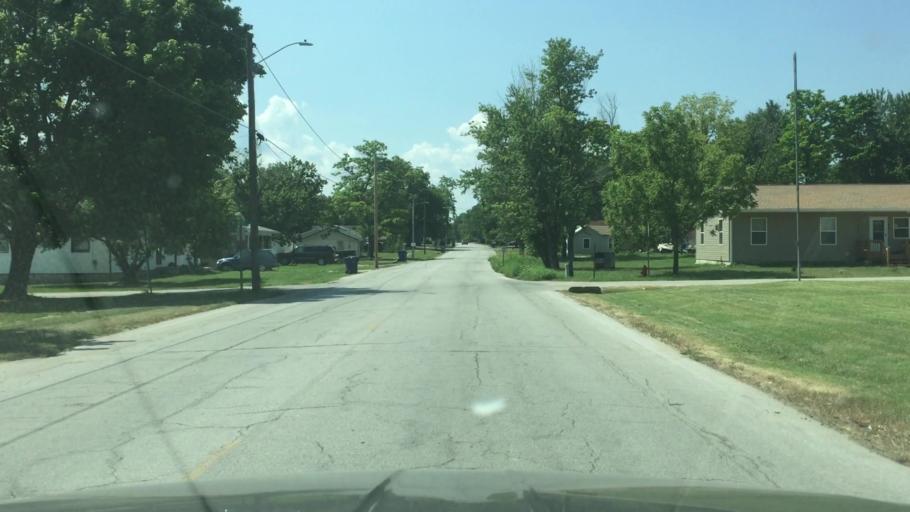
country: US
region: Missouri
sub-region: Miller County
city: Eldon
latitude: 38.3429
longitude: -92.5866
